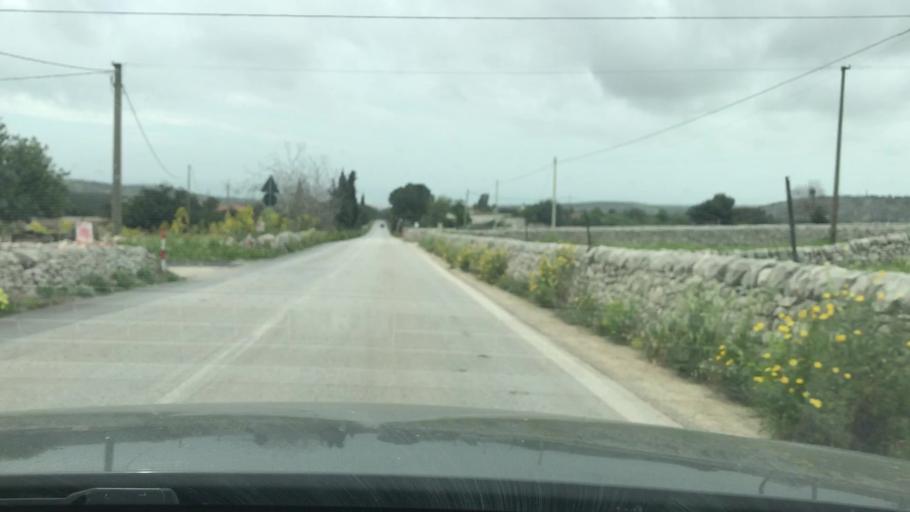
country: IT
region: Sicily
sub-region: Ragusa
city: Scicli
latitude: 36.8049
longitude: 14.7222
